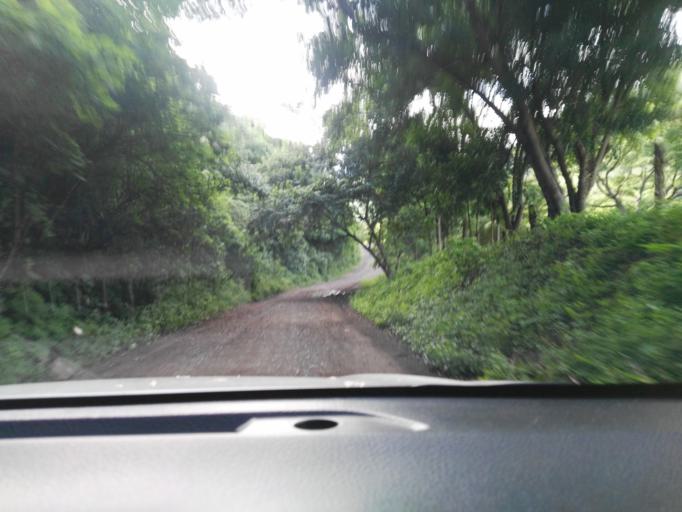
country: NI
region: Matagalpa
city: Terrabona
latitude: 12.8414
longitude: -86.0209
